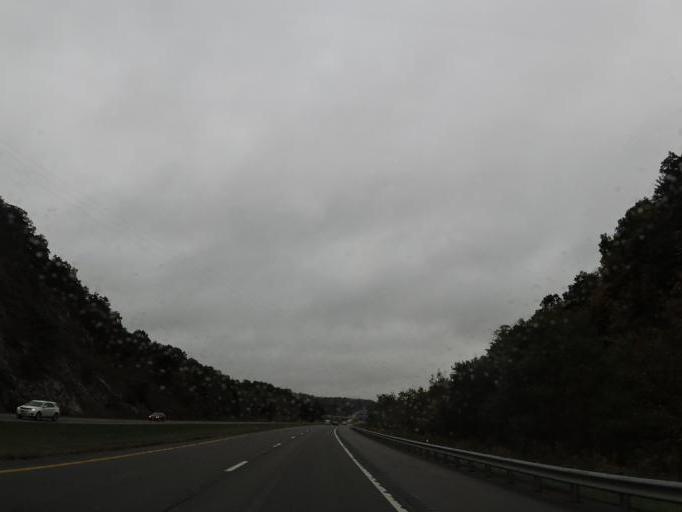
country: US
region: Virginia
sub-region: Wythe County
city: Wytheville
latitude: 36.9925
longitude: -81.0786
